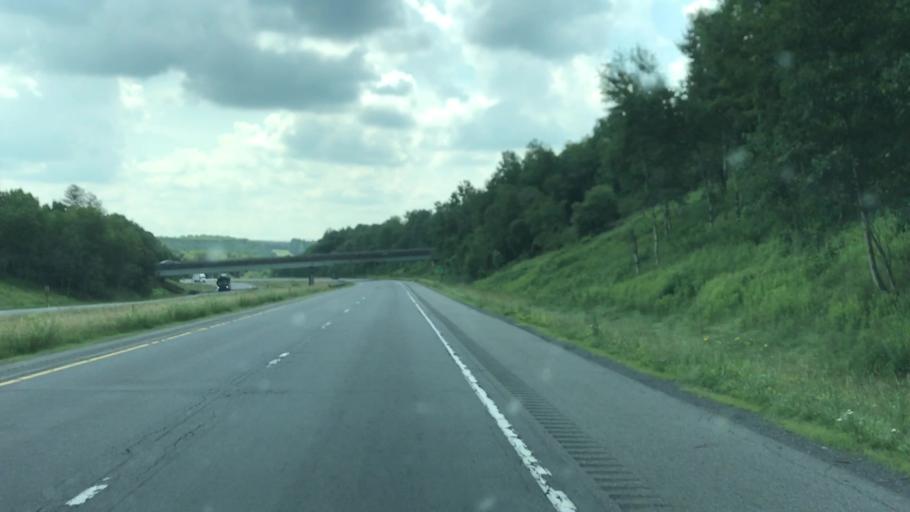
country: US
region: Pennsylvania
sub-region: Lackawanna County
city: Mount Cobb
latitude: 41.3731
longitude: -75.4507
